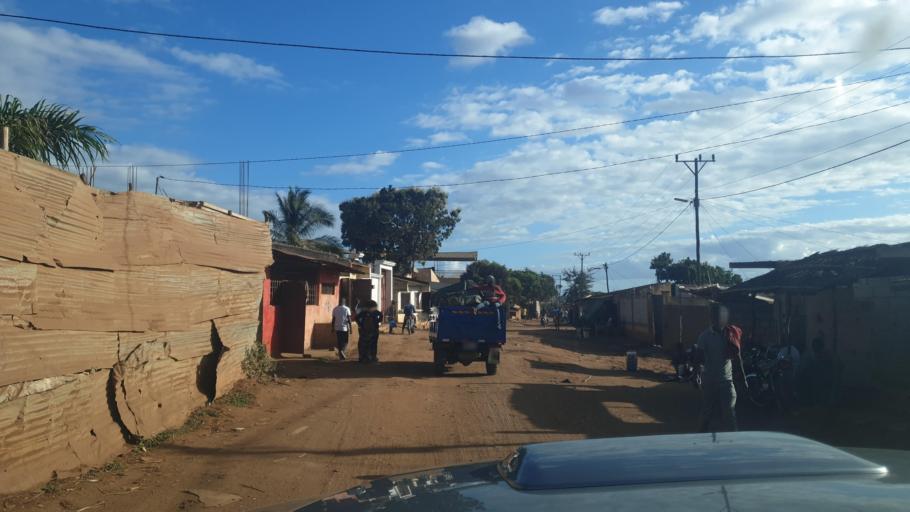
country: MZ
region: Nampula
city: Nampula
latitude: -15.1370
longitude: 39.2684
